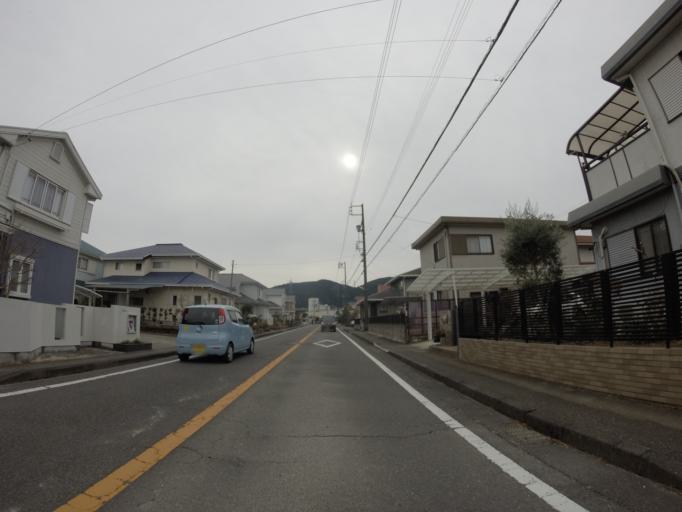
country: JP
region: Shizuoka
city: Fujinomiya
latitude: 35.1875
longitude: 138.6018
